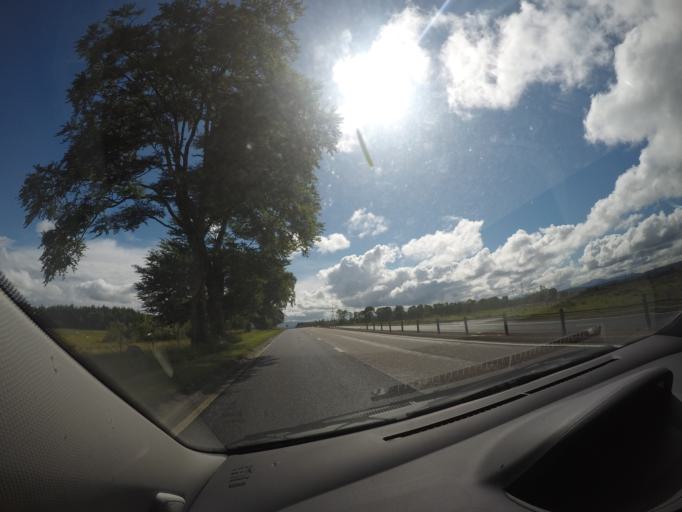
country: GB
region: Scotland
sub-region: Stirling
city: Dunblane
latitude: 56.2212
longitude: -3.9229
